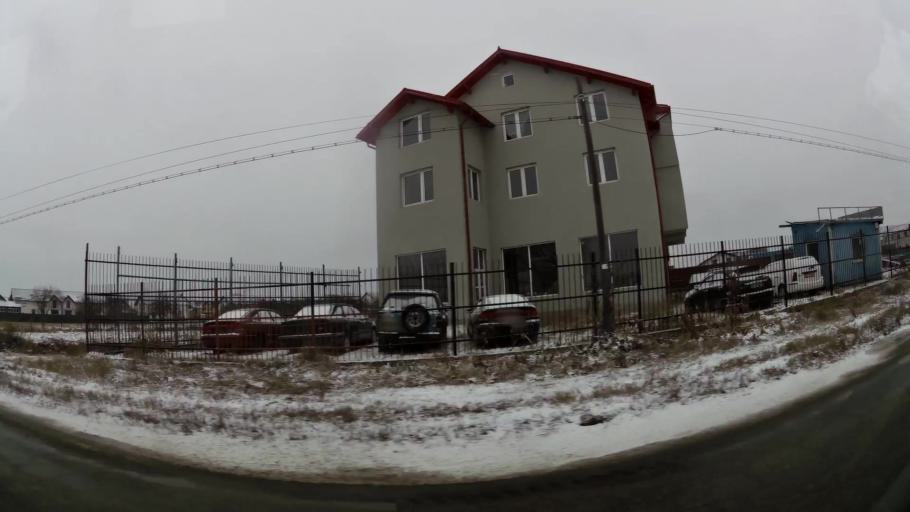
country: RO
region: Dambovita
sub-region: Comuna Ulmi
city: Ulmi
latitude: 44.8926
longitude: 25.5150
